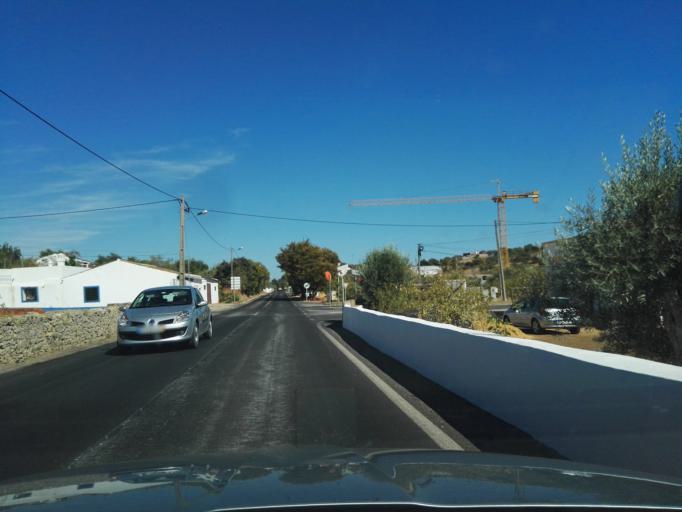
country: PT
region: Faro
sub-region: Sao Bras de Alportel
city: Sao Bras de Alportel
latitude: 37.1547
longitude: -7.8567
